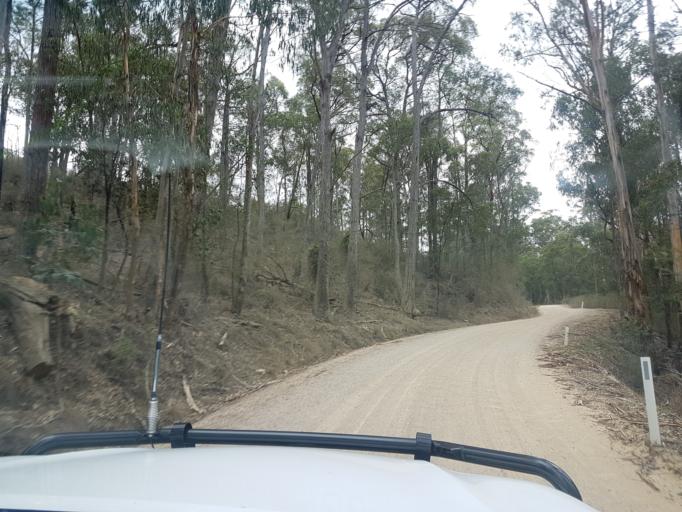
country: AU
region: Victoria
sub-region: East Gippsland
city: Bairnsdale
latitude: -37.6928
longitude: 147.5643
